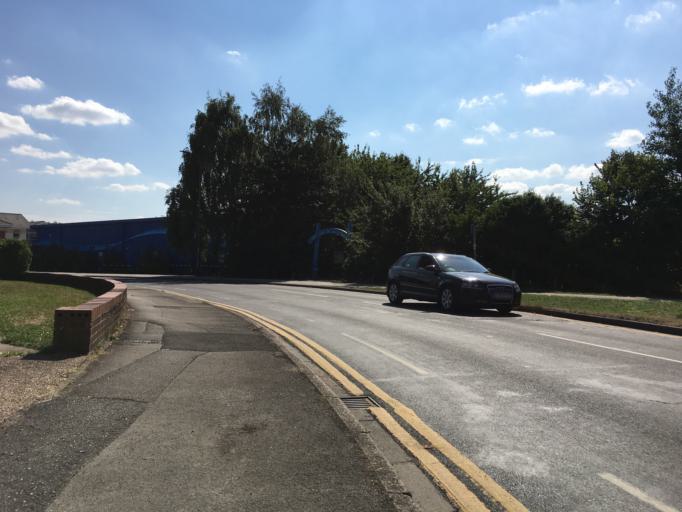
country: GB
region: England
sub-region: City of Kingston upon Hull
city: Hull
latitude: 53.7502
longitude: -0.3406
